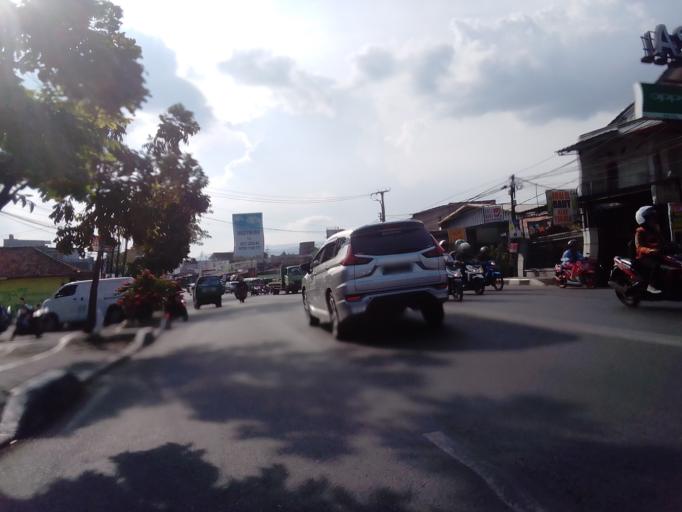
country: ID
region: West Java
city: Cileunyi
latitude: -6.9193
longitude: 107.7082
